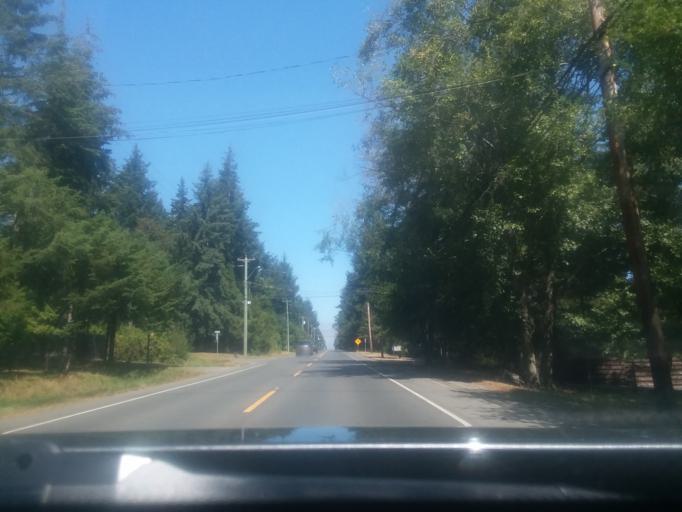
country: CA
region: British Columbia
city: Courtenay
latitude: 49.7040
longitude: -124.9341
